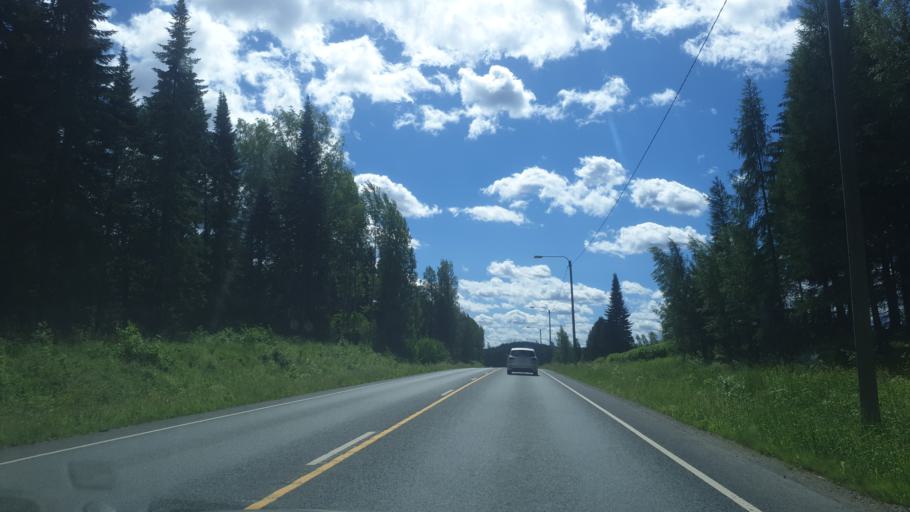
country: FI
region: Northern Savo
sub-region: Varkaus
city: Leppaevirta
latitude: 62.6441
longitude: 27.6078
